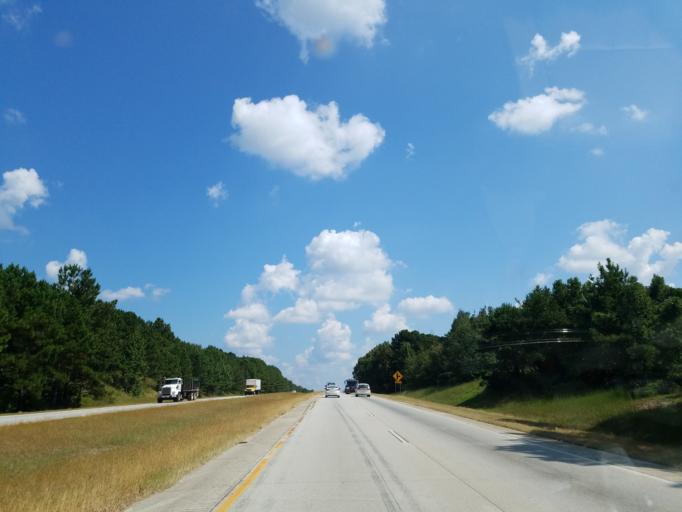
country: US
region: Georgia
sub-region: Gwinnett County
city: Dacula
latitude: 33.9734
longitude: -83.8804
